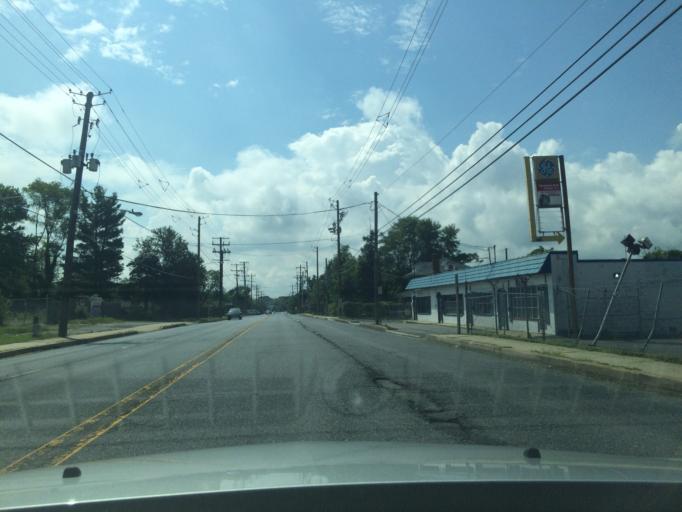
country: US
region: Maryland
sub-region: Prince George's County
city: Coral Hills
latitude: 38.8640
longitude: -76.9146
